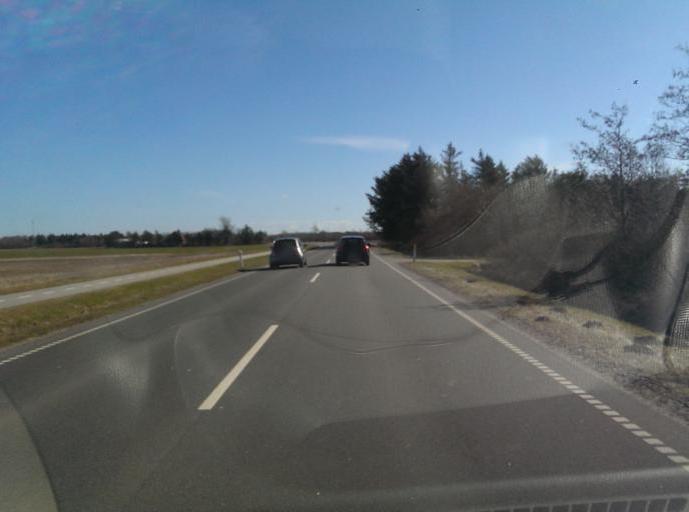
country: DK
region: Central Jutland
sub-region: Holstebro Kommune
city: Ulfborg
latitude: 56.2681
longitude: 8.2282
